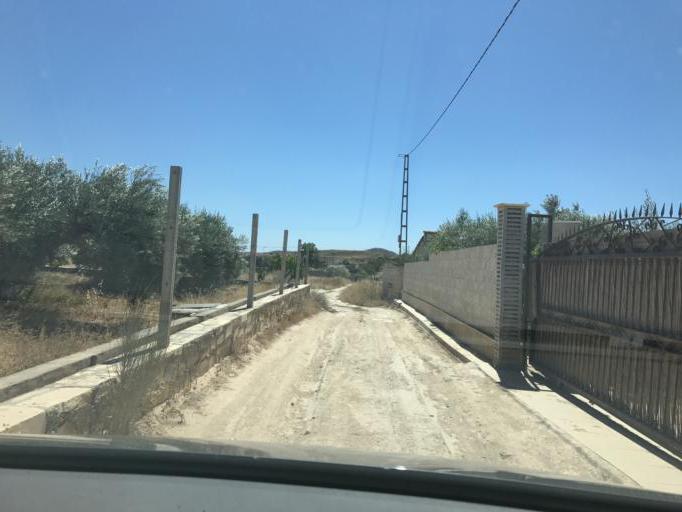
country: ES
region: Andalusia
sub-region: Provincia de Almeria
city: Fines
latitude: 37.3562
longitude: -2.2522
